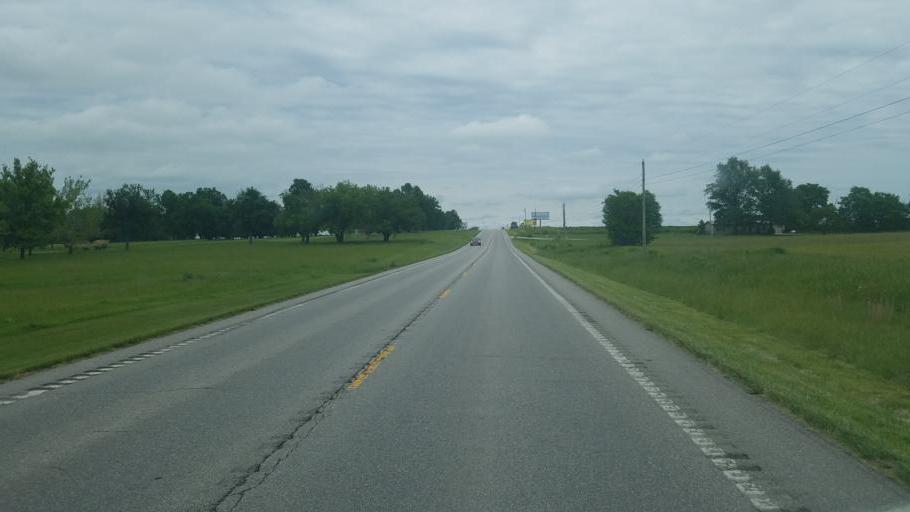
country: US
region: Missouri
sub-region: Morgan County
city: Versailles
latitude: 38.4656
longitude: -92.8089
